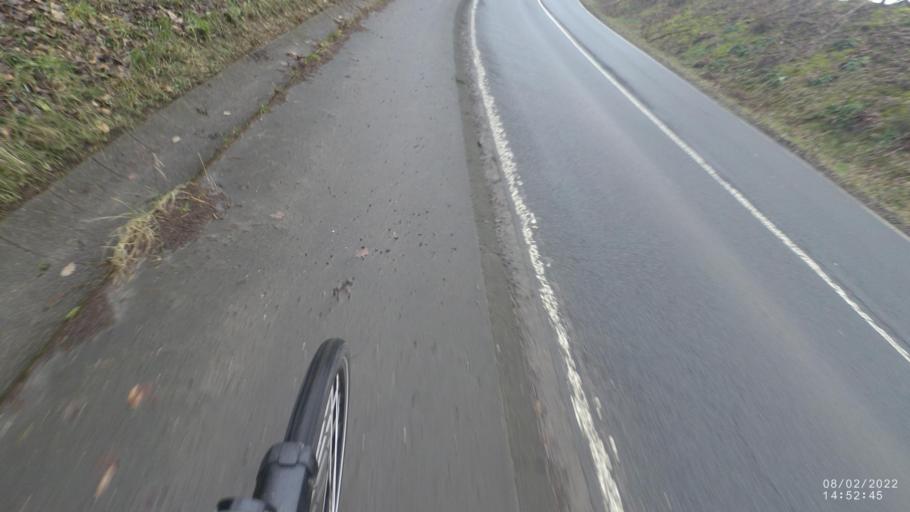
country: DE
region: North Rhine-Westphalia
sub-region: Regierungsbezirk Arnsberg
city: Schalksmuhle
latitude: 51.2556
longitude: 7.5614
